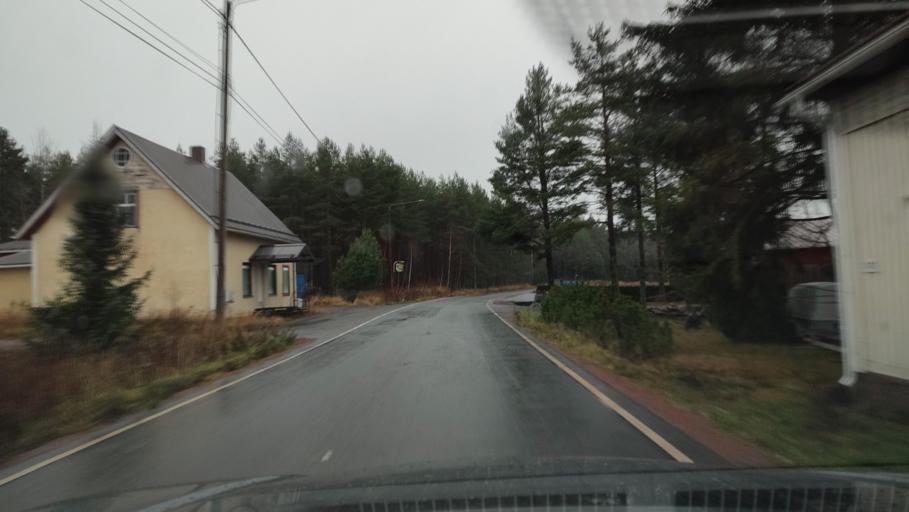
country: FI
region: Southern Ostrobothnia
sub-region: Suupohja
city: Karijoki
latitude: 62.1337
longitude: 21.6740
